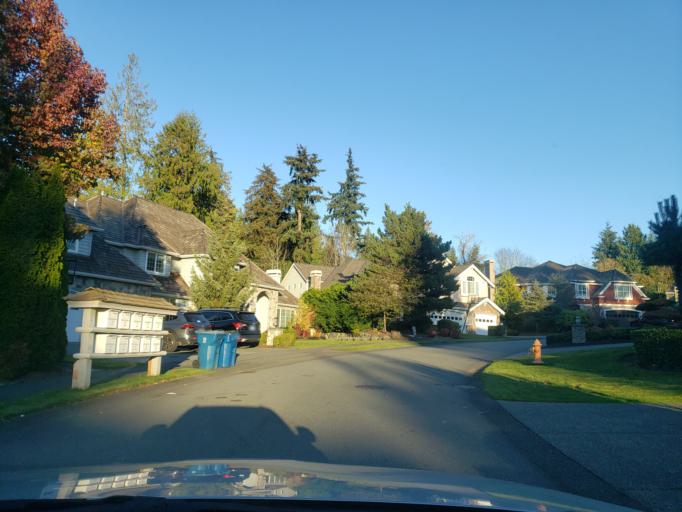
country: US
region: Washington
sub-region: Snohomish County
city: Woodway
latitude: 47.7847
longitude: -122.3791
